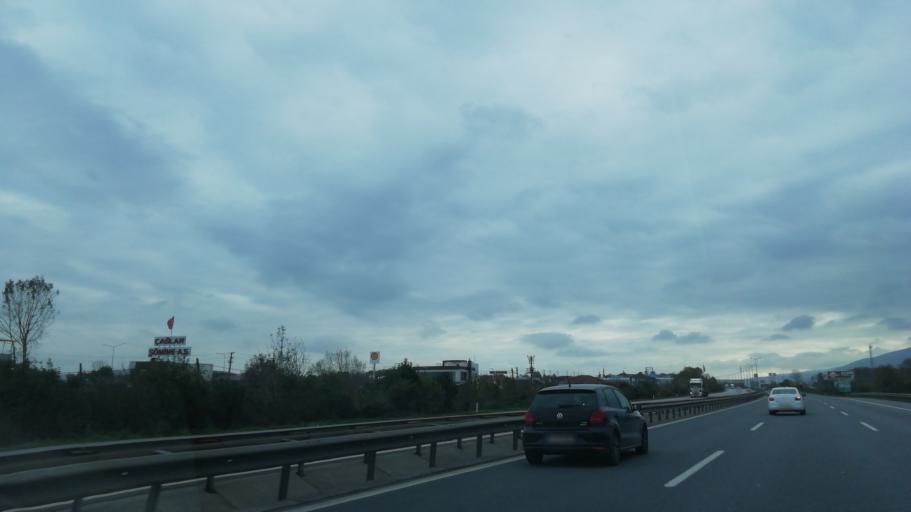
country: TR
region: Kocaeli
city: Derbent
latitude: 40.7307
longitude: 30.0598
